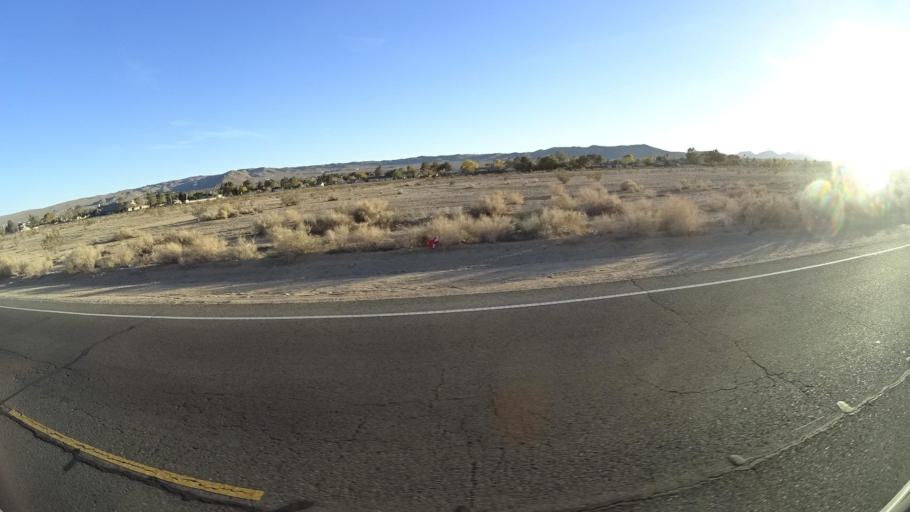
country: US
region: California
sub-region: Kern County
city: Ridgecrest
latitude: 35.6082
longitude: -117.6841
